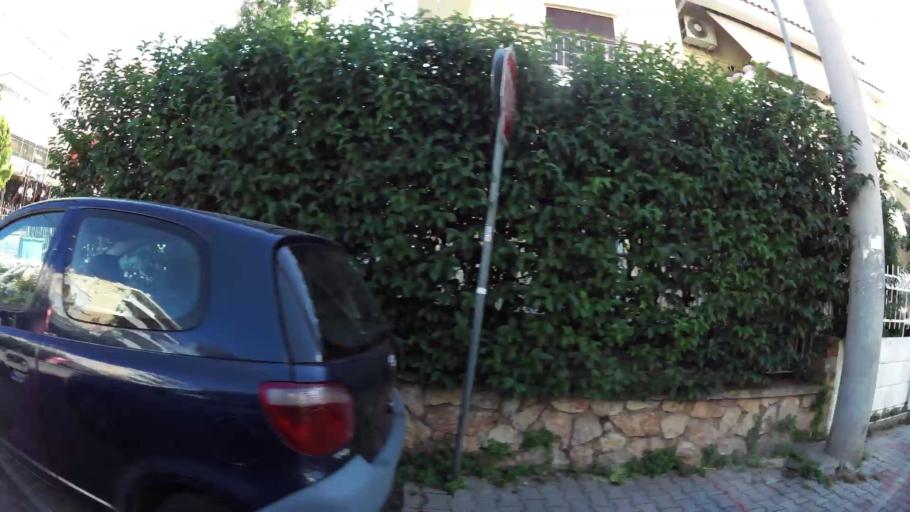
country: GR
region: Attica
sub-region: Nomarchia Athinas
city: Neo Psychiko
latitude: 38.0020
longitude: 23.7878
